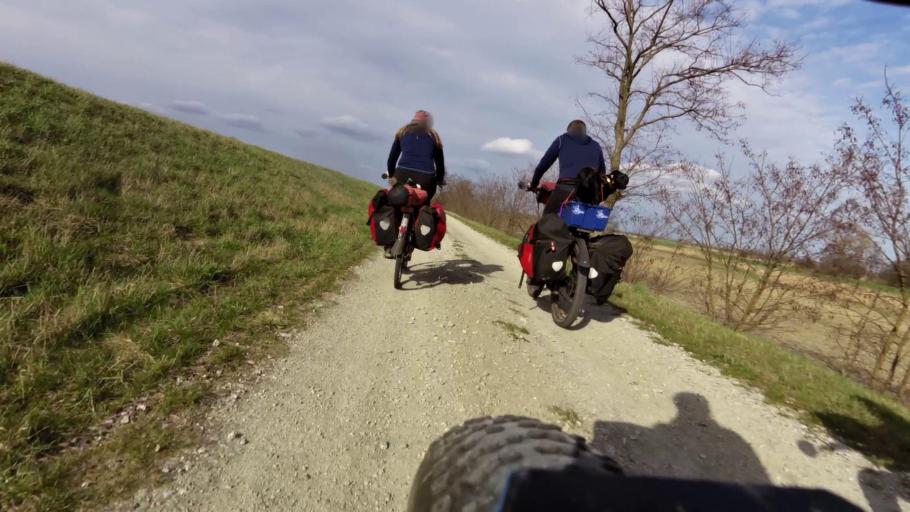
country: PL
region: Lubusz
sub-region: Powiat gorzowski
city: Kostrzyn nad Odra
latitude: 52.5438
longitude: 14.6186
